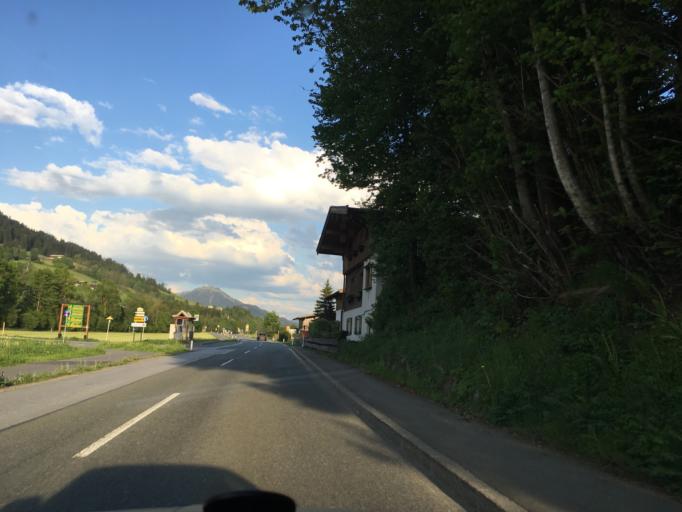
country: AT
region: Tyrol
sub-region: Politischer Bezirk Kitzbuhel
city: Sankt Johann in Tirol
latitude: 47.5085
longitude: 12.4658
